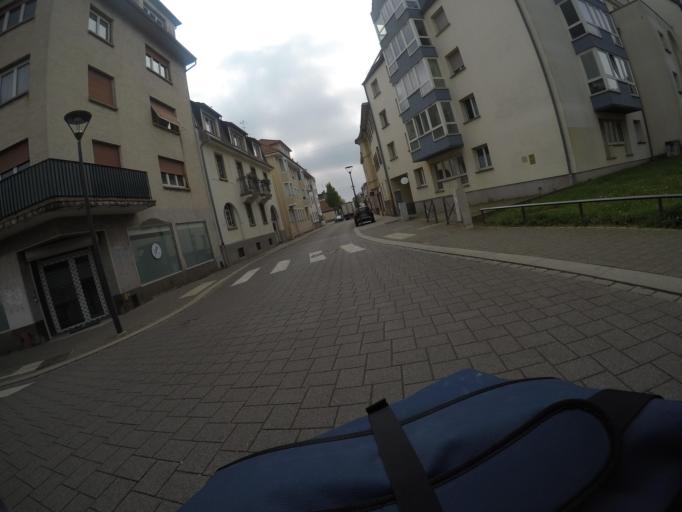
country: FR
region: Alsace
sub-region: Departement du Bas-Rhin
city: Strasbourg
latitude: 48.5934
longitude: 7.7215
